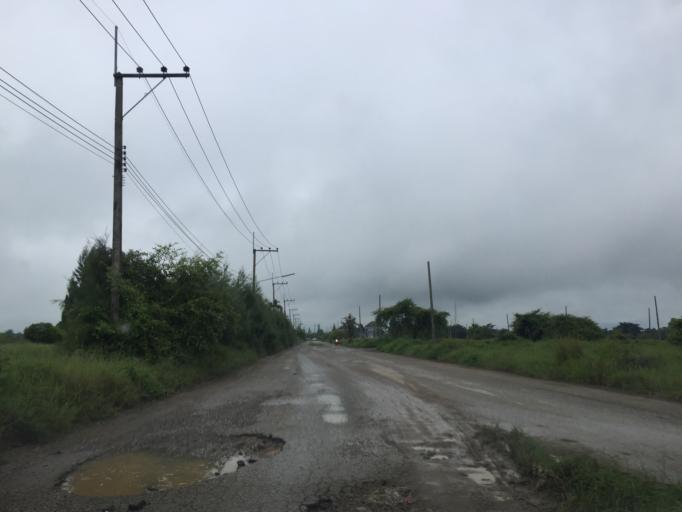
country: TH
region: Lamphun
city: Ban Thi
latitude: 18.6732
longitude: 99.1012
